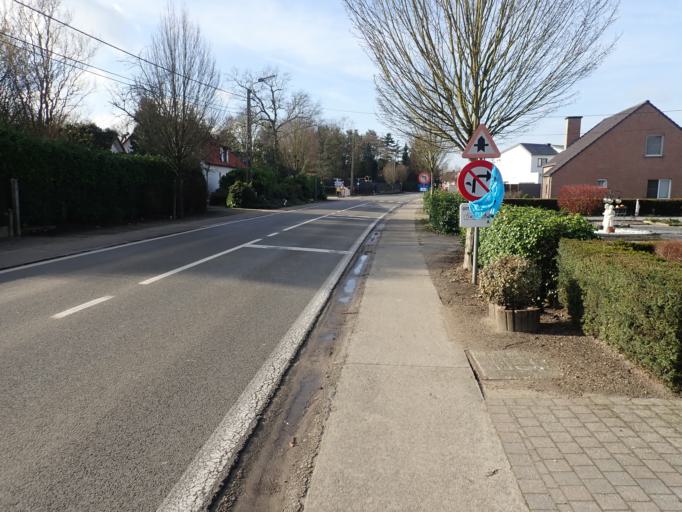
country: BE
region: Flanders
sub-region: Provincie Vlaams-Brabant
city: Keerbergen
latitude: 51.0086
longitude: 4.6490
